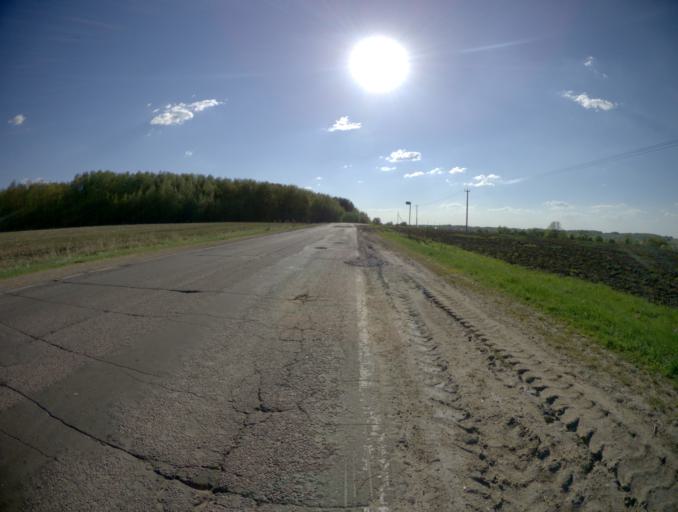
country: RU
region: Ivanovo
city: Gavrilov Posad
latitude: 56.3463
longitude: 40.1713
